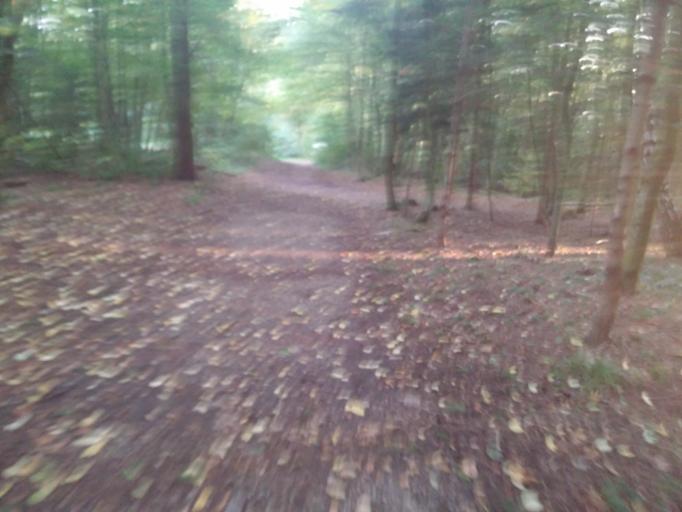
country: DE
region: Bavaria
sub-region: Upper Bavaria
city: Vaterstetten
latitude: 48.1058
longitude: 11.7503
